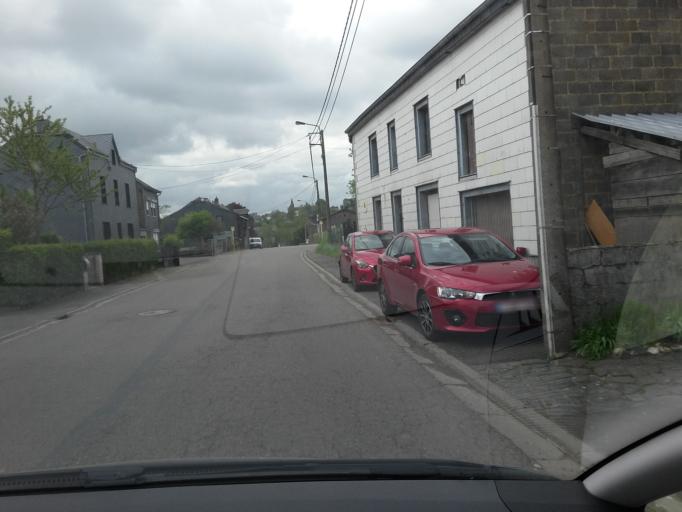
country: BE
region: Wallonia
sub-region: Province du Luxembourg
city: Bertrix
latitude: 49.8238
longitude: 5.3225
